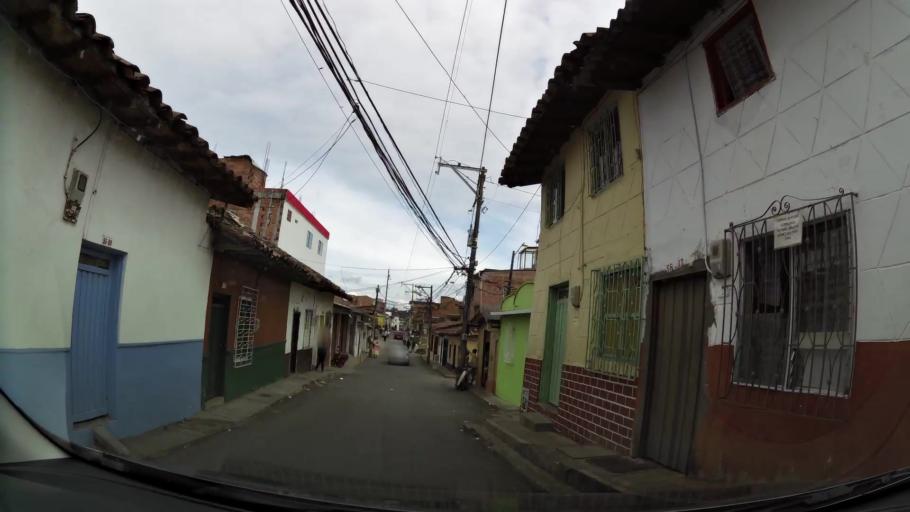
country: CO
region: Antioquia
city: Rionegro
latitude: 6.1554
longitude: -75.3771
